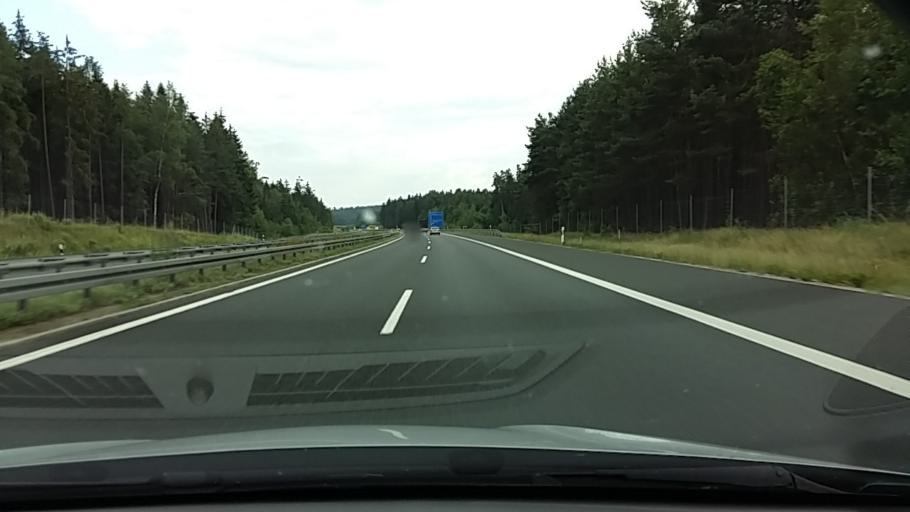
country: DE
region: Bavaria
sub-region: Upper Palatinate
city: Wernberg-Koblitz
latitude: 49.5499
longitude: 12.1944
